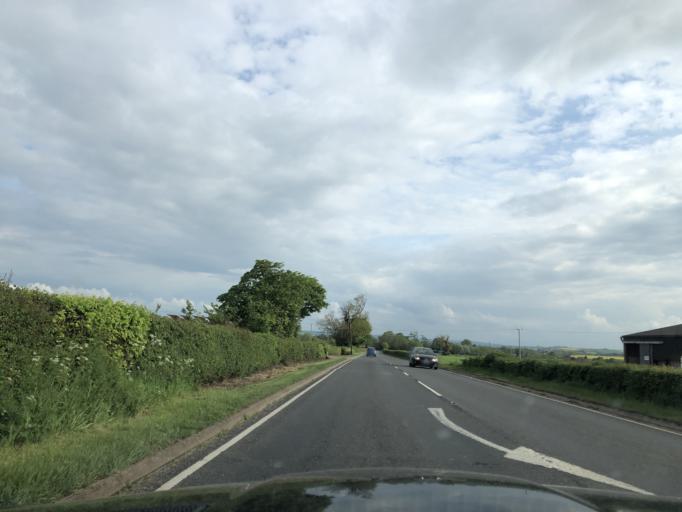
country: GB
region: England
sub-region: Warwickshire
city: Shipston on Stour
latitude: 52.1194
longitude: -1.6203
